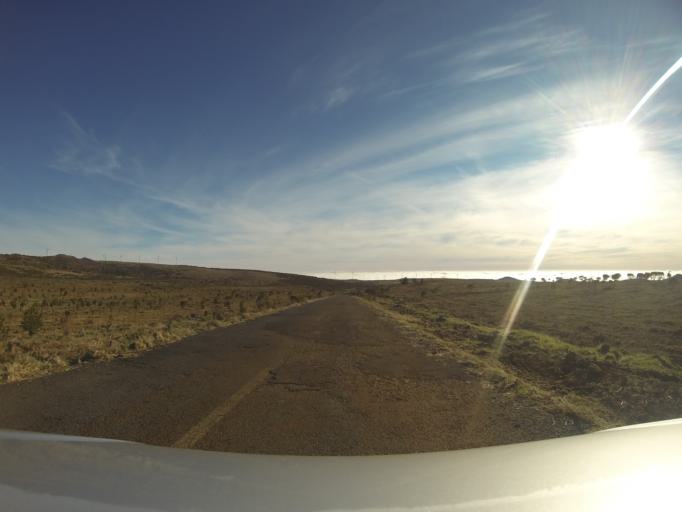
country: PT
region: Madeira
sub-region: Sao Vicente
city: Sao Vicente
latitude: 32.7661
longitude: -17.0810
